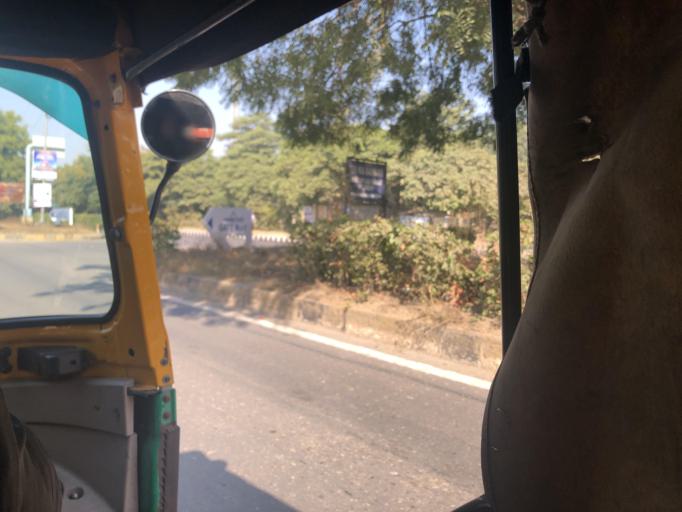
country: IN
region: Haryana
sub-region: Gurgaon
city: Gurgaon
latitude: 28.4451
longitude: 77.0820
